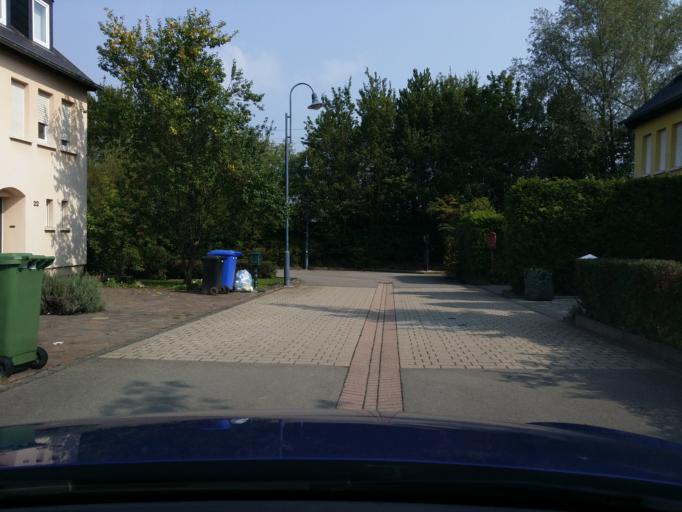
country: LU
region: Luxembourg
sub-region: Canton de Luxembourg
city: Bertrange
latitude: 49.6134
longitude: 6.0563
